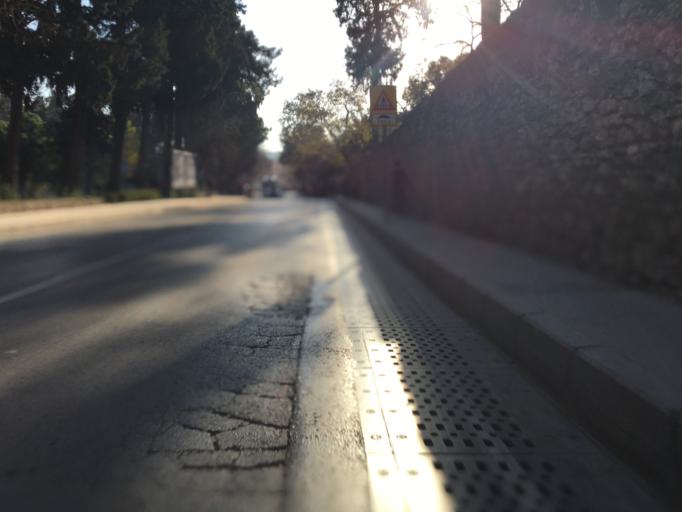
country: TR
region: Izmir
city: Buca
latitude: 38.3842
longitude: 27.1775
